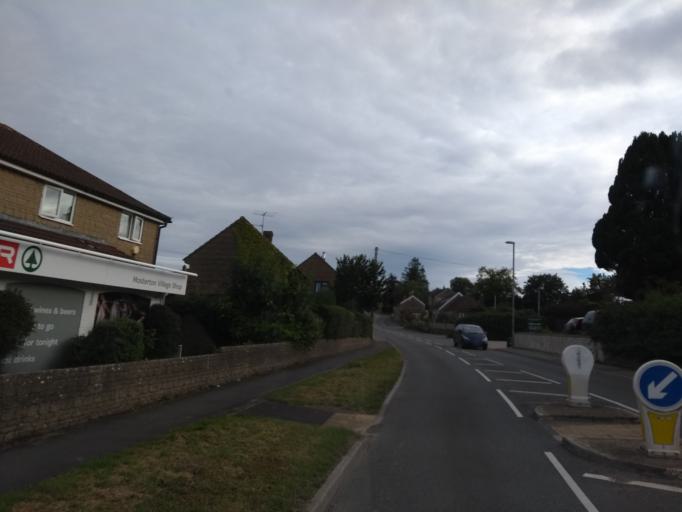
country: GB
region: England
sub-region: Somerset
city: Crewkerne
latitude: 50.8447
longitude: -2.7720
